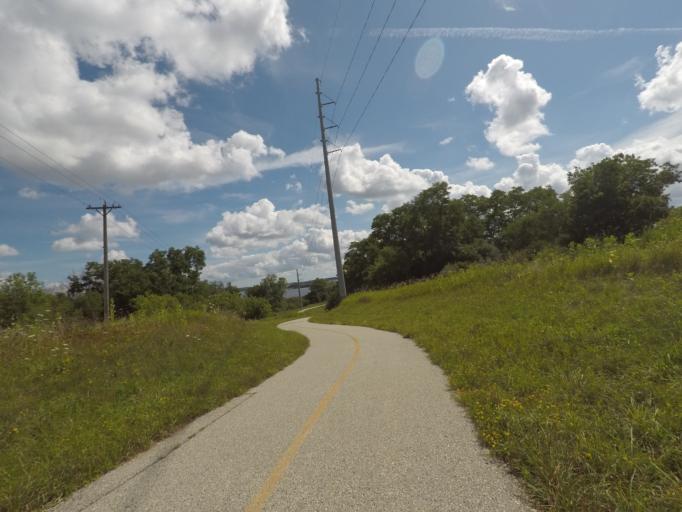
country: US
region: Wisconsin
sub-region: Waukesha County
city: Hartland
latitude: 43.0572
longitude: -88.3536
